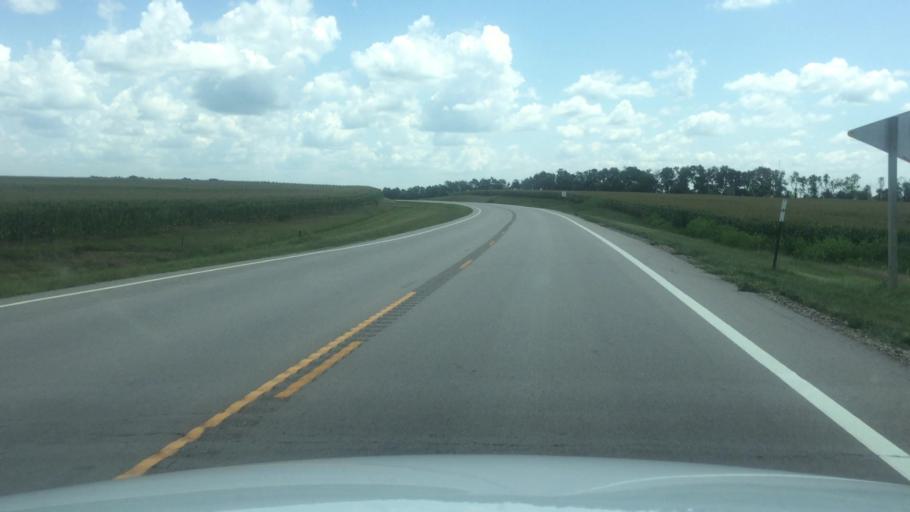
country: US
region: Kansas
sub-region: Brown County
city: Horton
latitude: 39.6629
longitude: -95.4139
